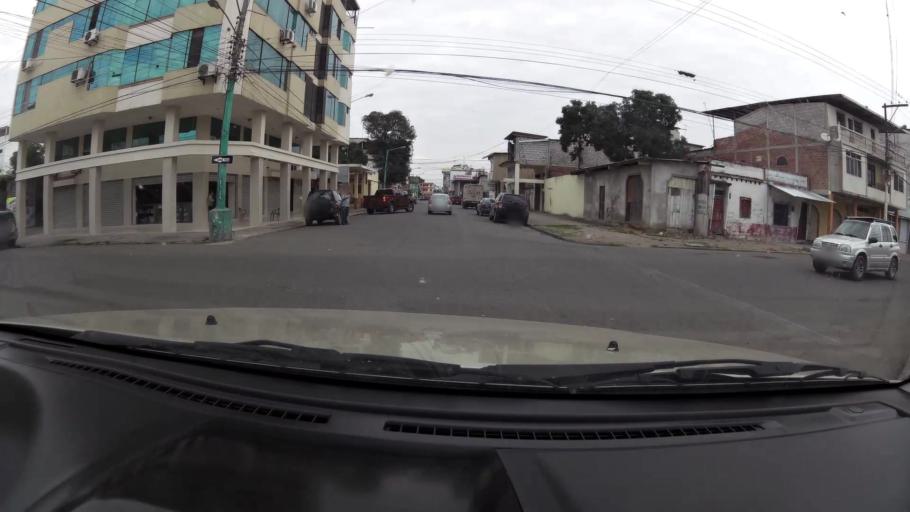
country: EC
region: El Oro
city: Machala
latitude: -3.2629
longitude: -79.9519
